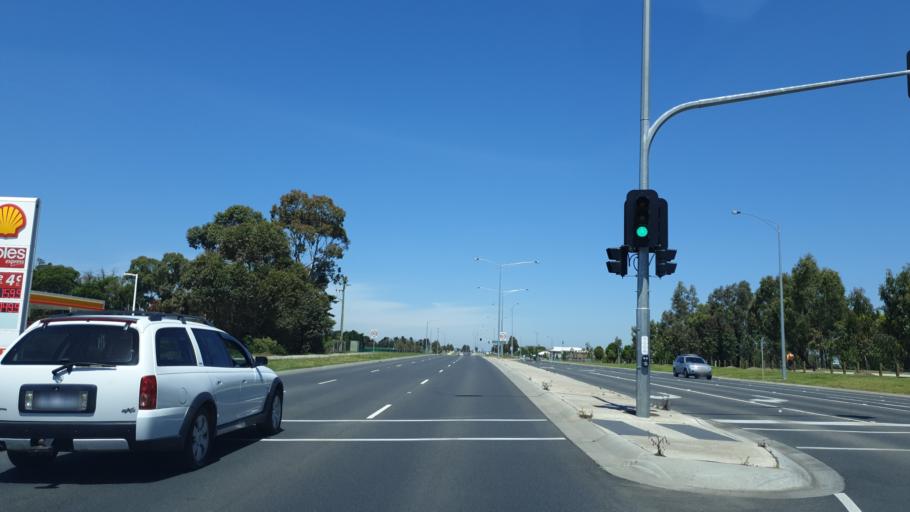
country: AU
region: Victoria
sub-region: Casey
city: Cranbourne North
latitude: -38.0689
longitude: 145.2985
